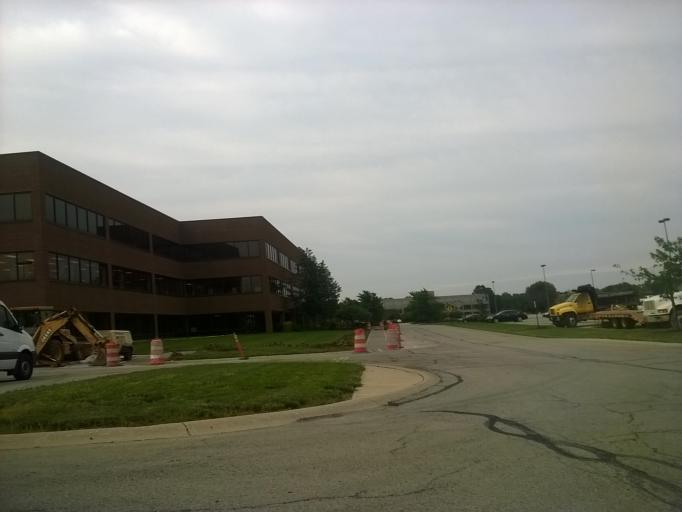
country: US
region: Indiana
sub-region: Hamilton County
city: Carmel
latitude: 39.9611
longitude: -86.1499
